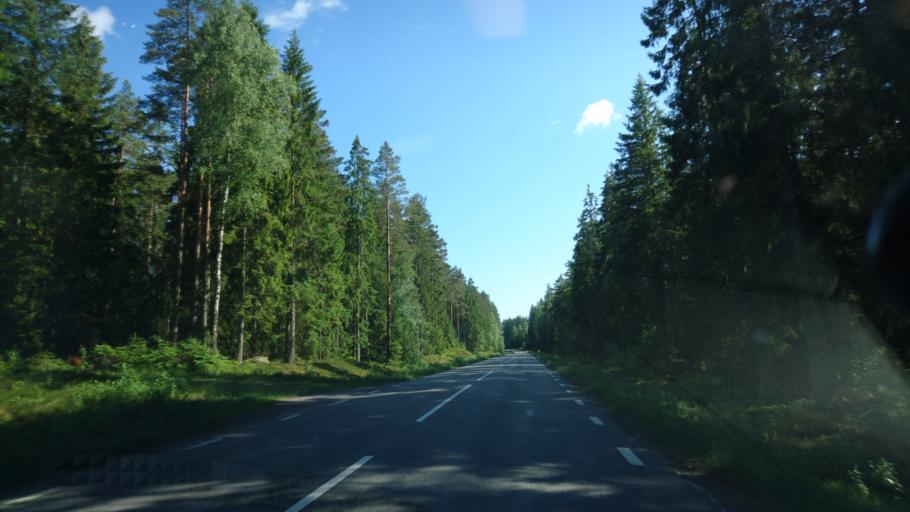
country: SE
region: Skane
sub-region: Osby Kommun
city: Lonsboda
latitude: 56.4583
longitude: 14.2335
